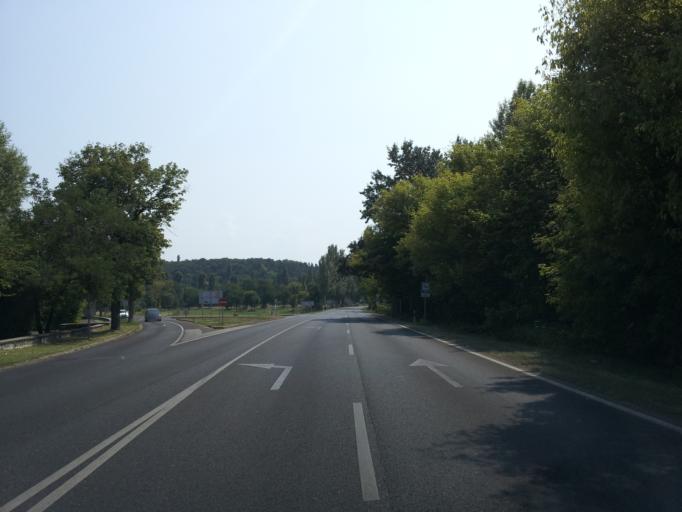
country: HU
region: Veszprem
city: Tihany
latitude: 46.9293
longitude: 17.8595
